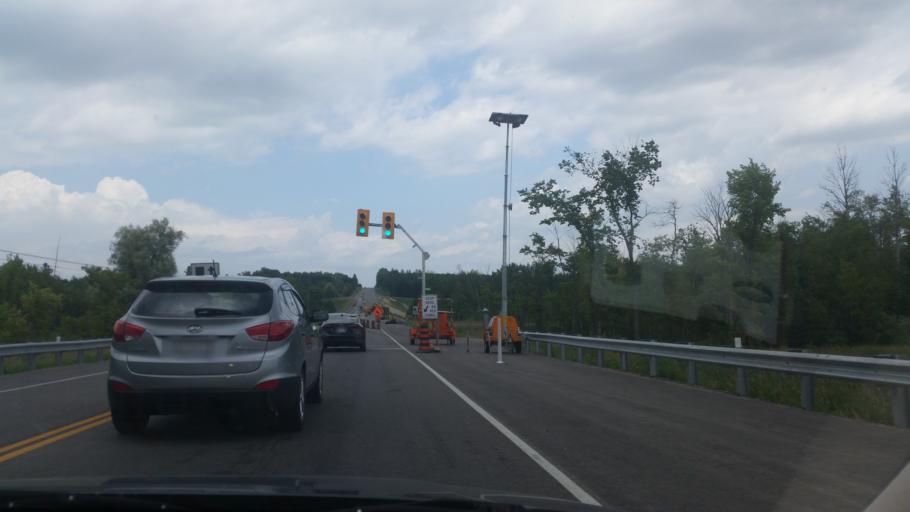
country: CA
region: Ontario
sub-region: Wellington County
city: Guelph
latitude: 43.7041
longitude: -80.1270
